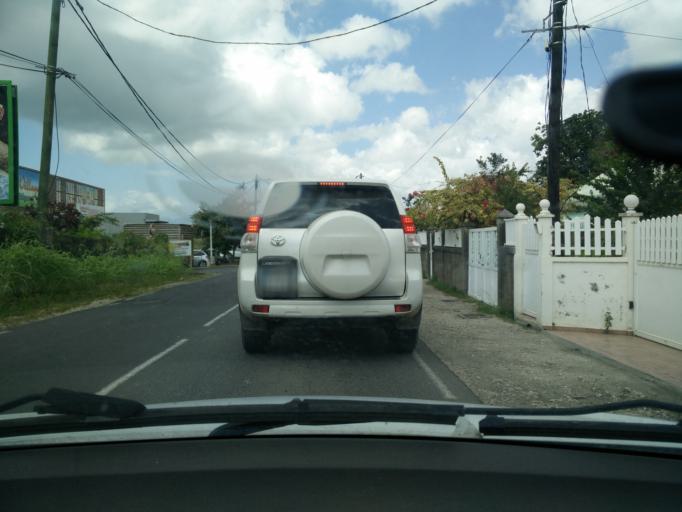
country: GP
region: Guadeloupe
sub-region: Guadeloupe
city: Les Abymes
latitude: 16.2600
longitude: -61.5076
